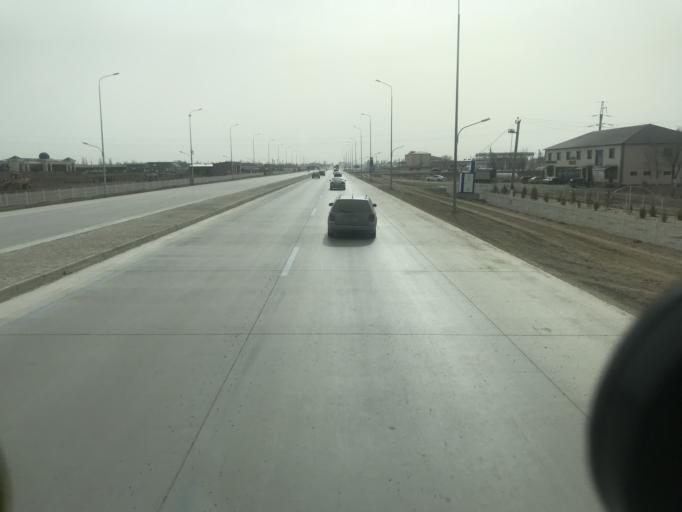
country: KZ
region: Ongtustik Qazaqstan
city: Turkestan
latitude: 43.2663
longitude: 68.3610
